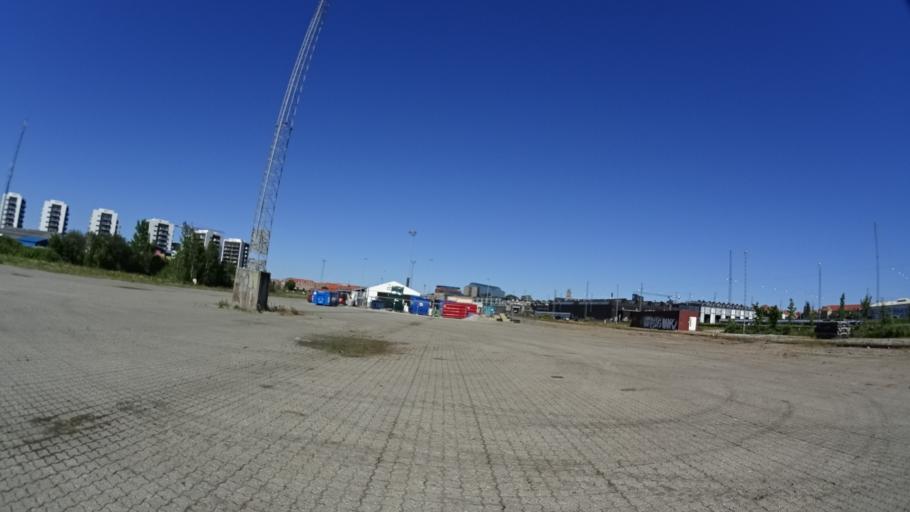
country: DK
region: Central Jutland
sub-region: Arhus Kommune
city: Arhus
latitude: 56.1503
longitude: 10.1867
